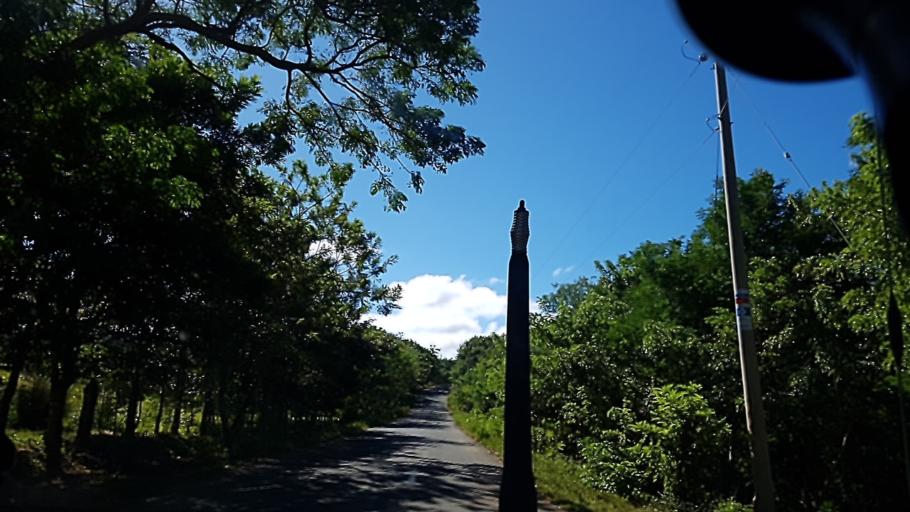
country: NI
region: Carazo
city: Santa Teresa
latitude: 11.6731
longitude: -86.1827
